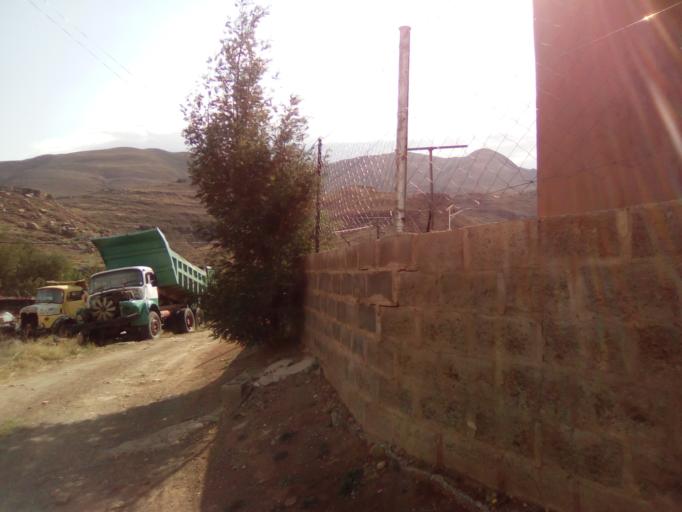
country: LS
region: Qacha's Nek
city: Qacha's Nek
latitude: -30.0969
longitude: 28.6501
